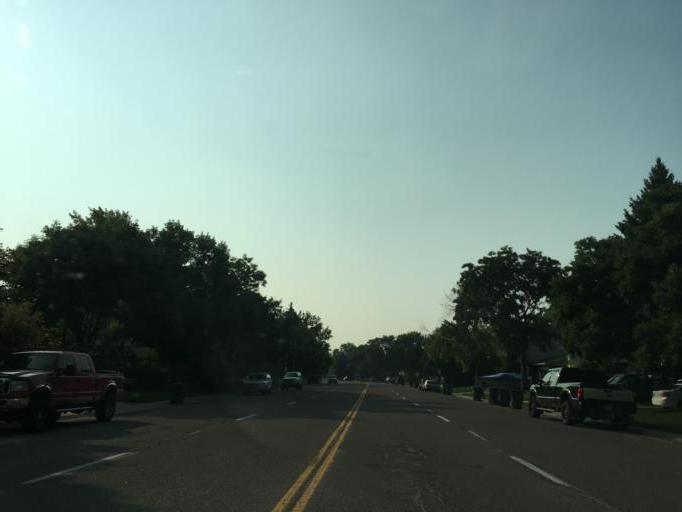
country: US
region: Colorado
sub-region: Adams County
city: Northglenn
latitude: 39.8800
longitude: -104.9915
